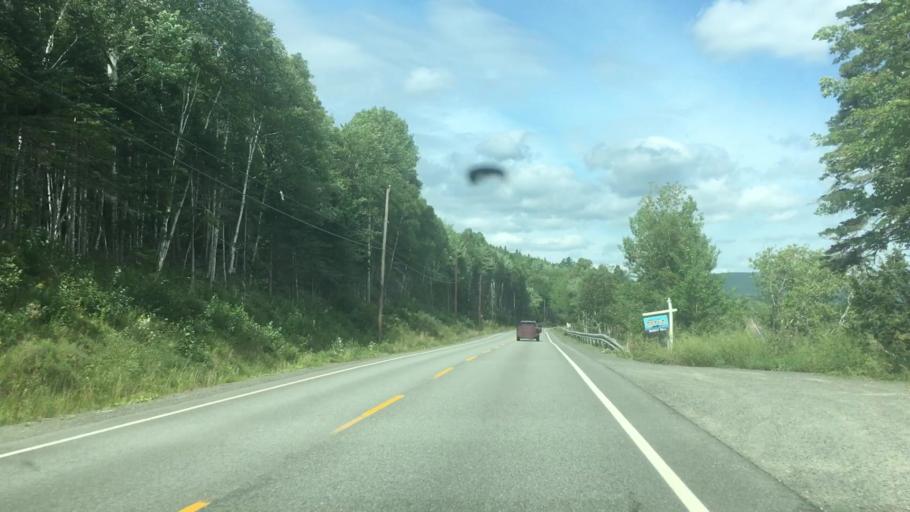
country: CA
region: Nova Scotia
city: Sydney Mines
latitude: 46.2747
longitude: -60.6110
